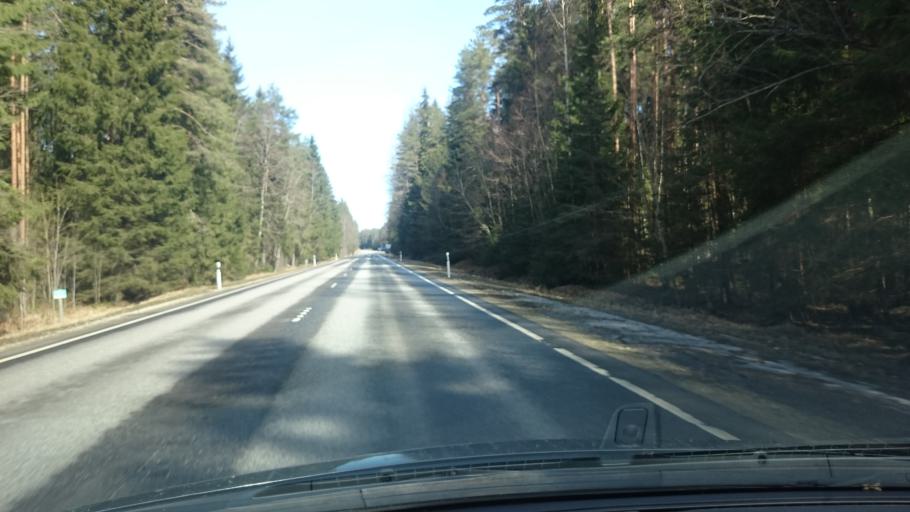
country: EE
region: Jaervamaa
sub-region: Tueri vald
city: Sarevere
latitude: 58.6928
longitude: 25.2501
